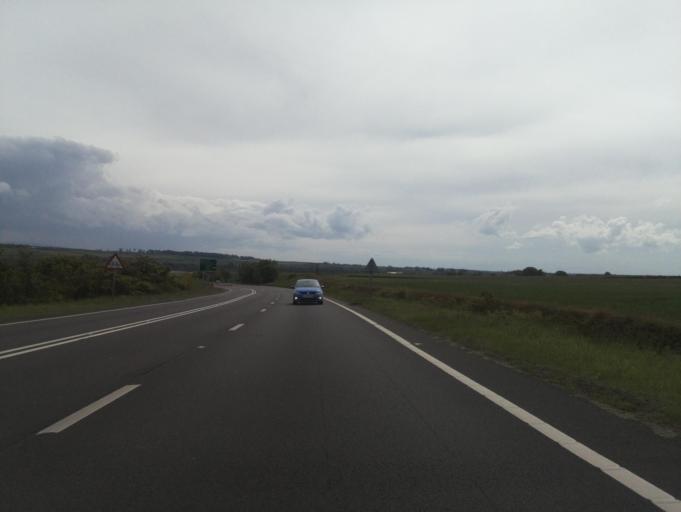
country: GB
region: England
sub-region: Northumberland
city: Berwick-Upon-Tweed
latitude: 55.7730
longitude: -2.0409
